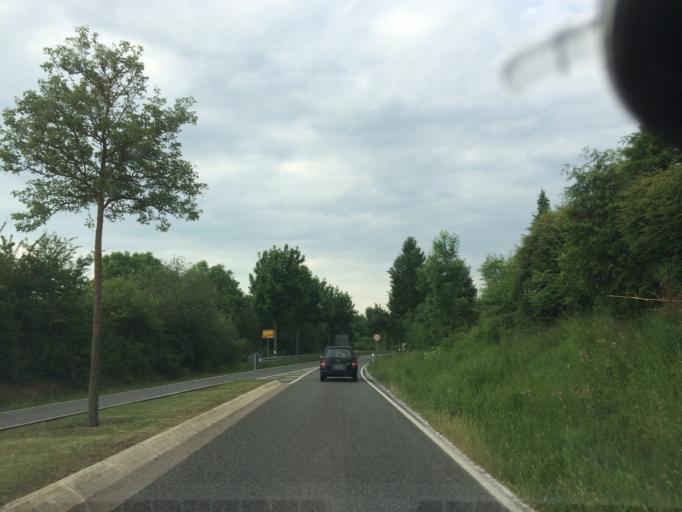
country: DE
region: Hesse
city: Trendelburg
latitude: 51.5642
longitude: 9.4175
